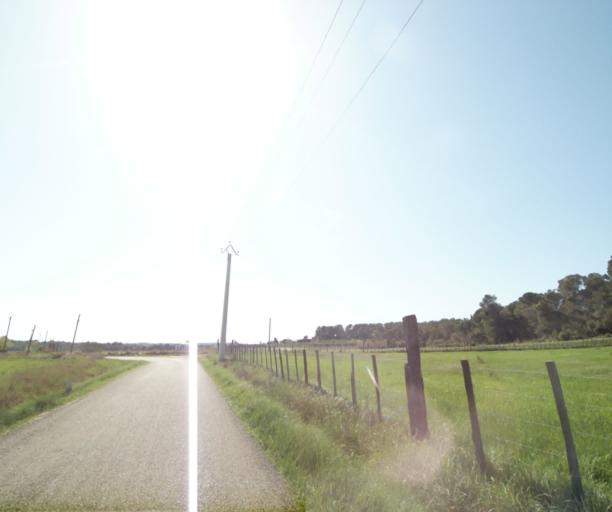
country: FR
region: Languedoc-Roussillon
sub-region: Departement de l'Herault
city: Saint-Drezery
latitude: 43.7075
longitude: 3.9692
